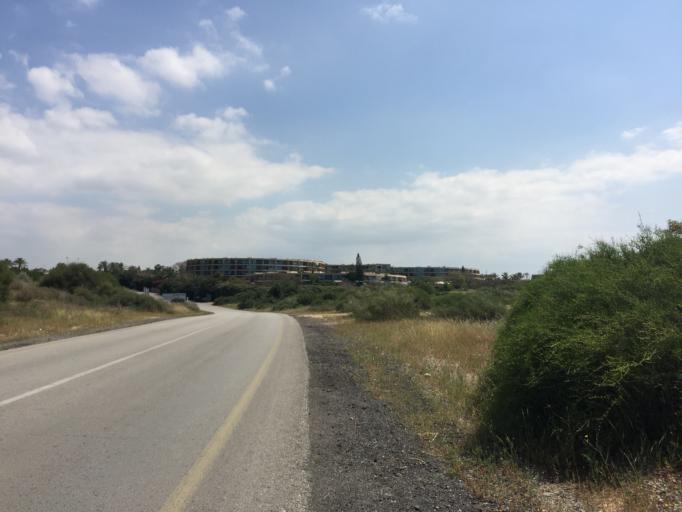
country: IL
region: Haifa
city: Qesarya
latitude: 32.4916
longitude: 34.8997
